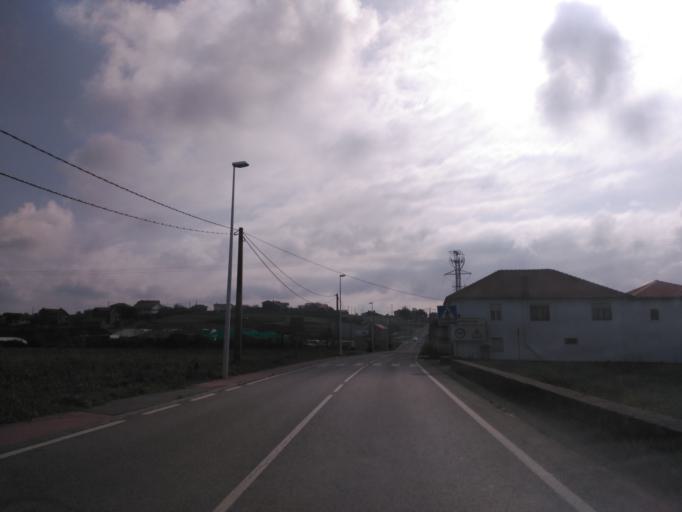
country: ES
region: Cantabria
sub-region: Provincia de Cantabria
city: Suances
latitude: 43.4199
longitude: -4.0688
